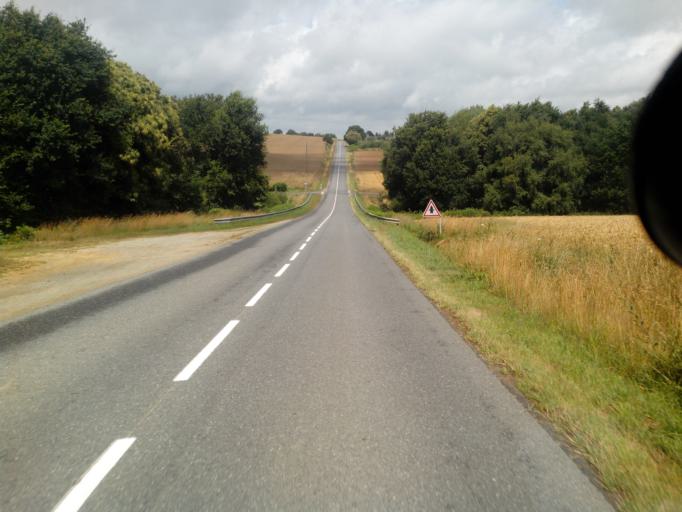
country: FR
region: Brittany
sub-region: Departement du Morbihan
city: Meneac
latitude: 48.1559
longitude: -2.4451
